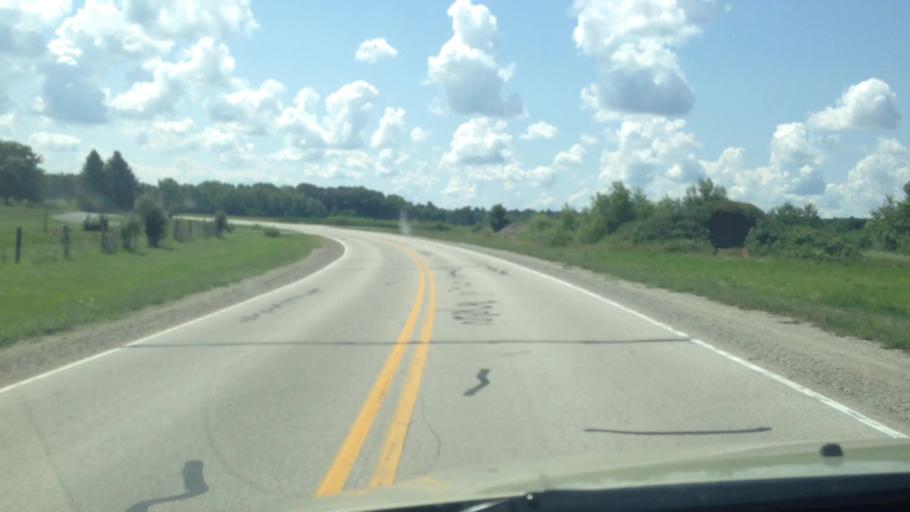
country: US
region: Wisconsin
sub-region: Brown County
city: Suamico
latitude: 44.6579
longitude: -88.0536
